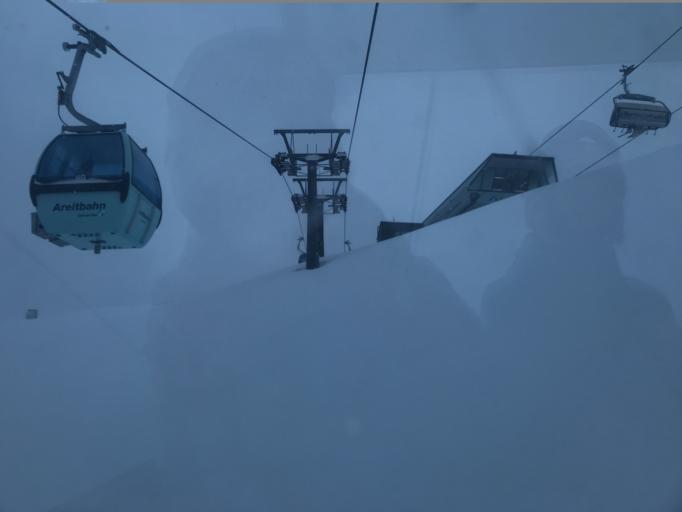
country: AT
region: Salzburg
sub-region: Politischer Bezirk Zell am See
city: Viehhofen
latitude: 47.3234
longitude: 12.7375
